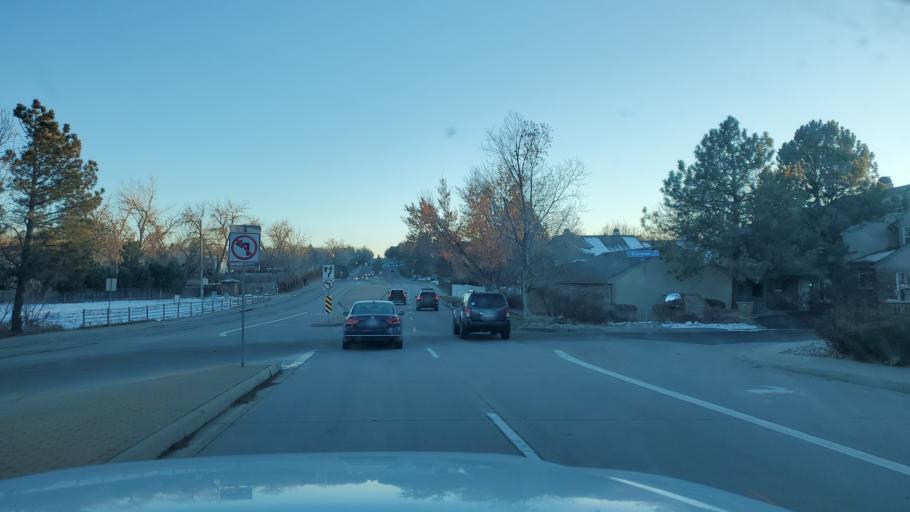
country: US
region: Colorado
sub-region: Arapahoe County
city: Castlewood
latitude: 39.5942
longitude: -104.9042
